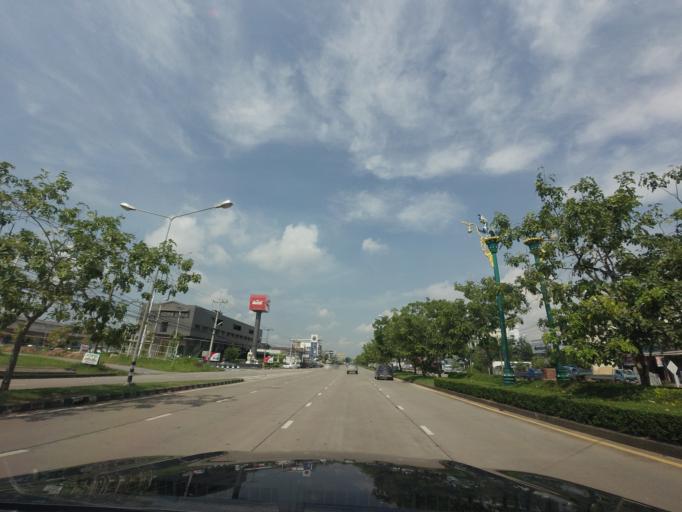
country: TH
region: Khon Kaen
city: Khon Kaen
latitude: 16.4423
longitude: 102.8096
